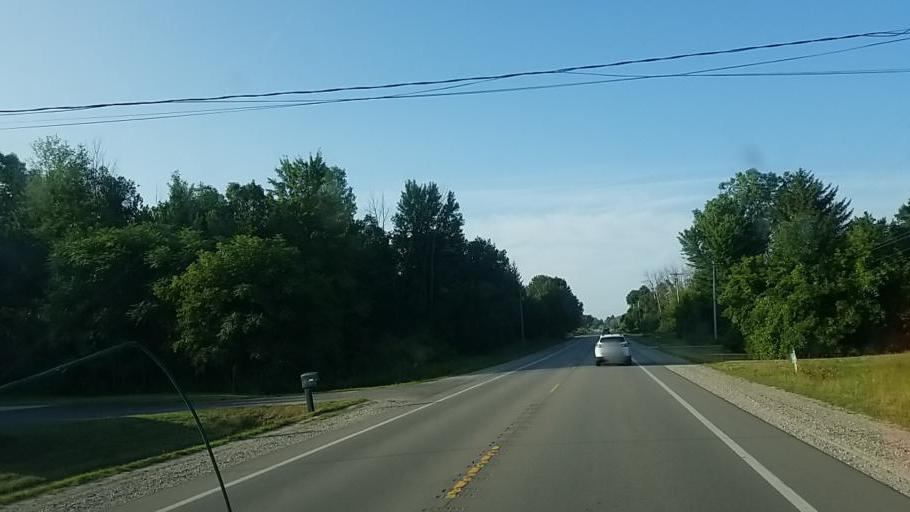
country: US
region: Michigan
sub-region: Montcalm County
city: Stanton
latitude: 43.2307
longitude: -85.0735
